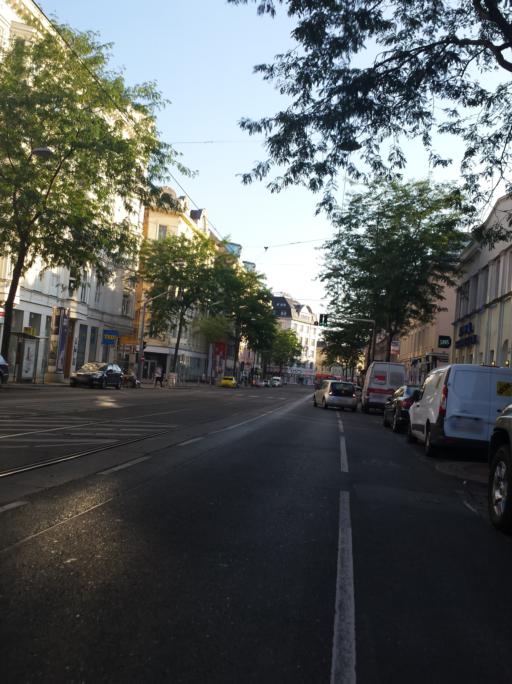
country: AT
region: Vienna
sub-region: Wien Stadt
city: Vienna
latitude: 48.1933
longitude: 16.3339
